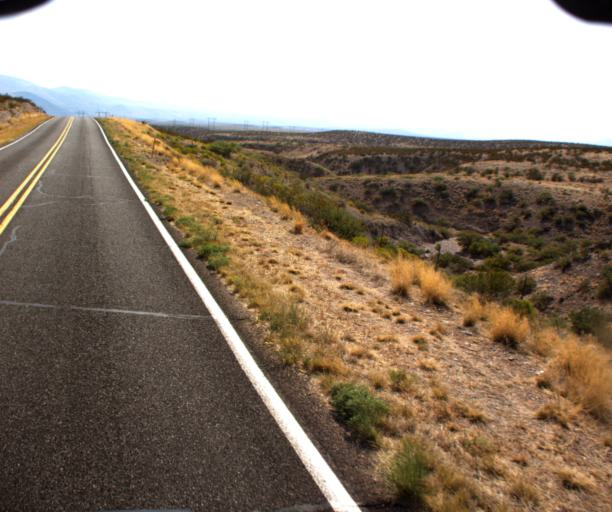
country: US
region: Arizona
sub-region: Greenlee County
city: Clifton
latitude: 32.9838
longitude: -109.1833
